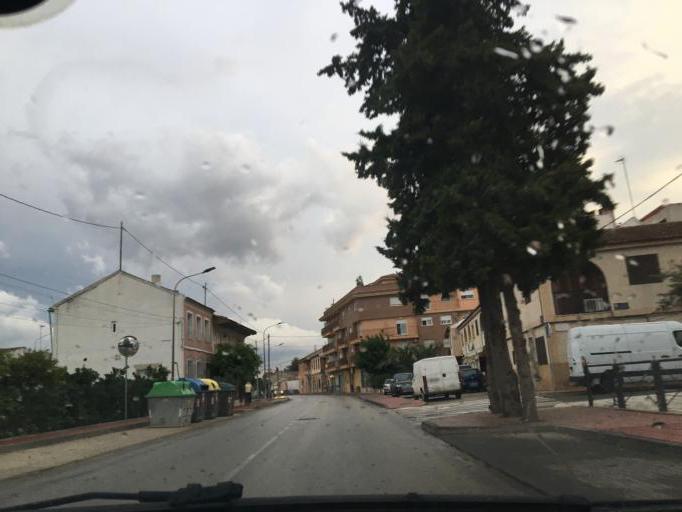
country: ES
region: Murcia
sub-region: Murcia
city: Santomera
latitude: 38.0187
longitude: -1.0498
